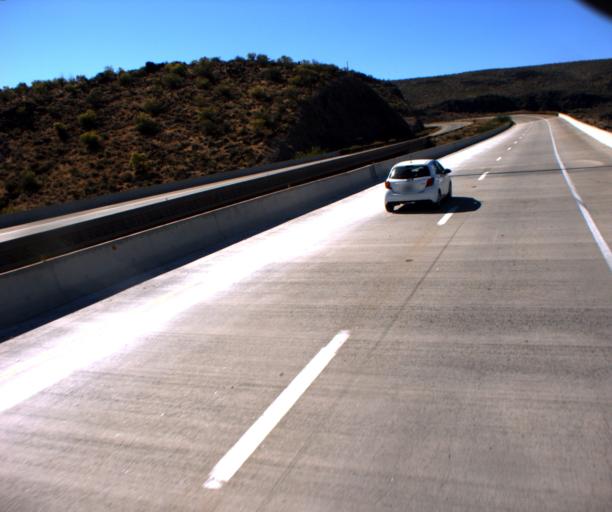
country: US
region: Arizona
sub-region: Yavapai County
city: Bagdad
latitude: 34.5773
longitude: -113.4905
